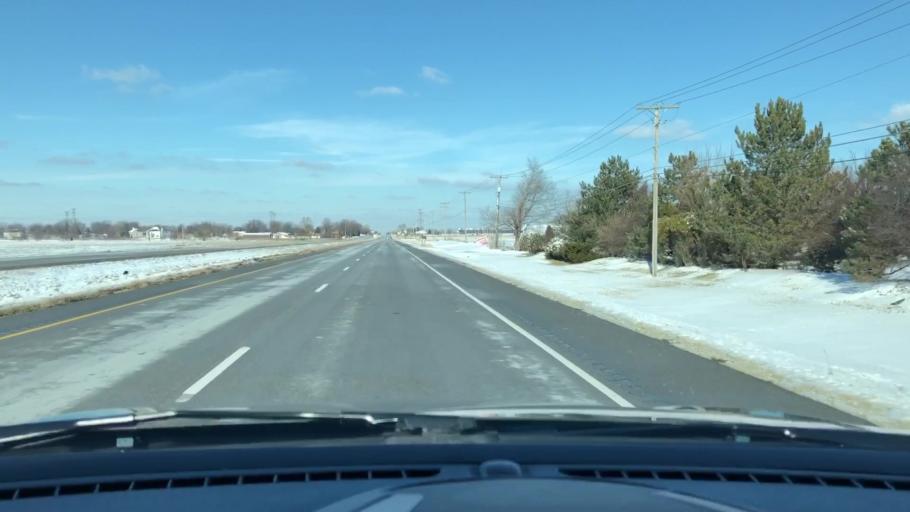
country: US
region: Illinois
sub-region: Will County
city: Elwood
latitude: 41.4399
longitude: -88.0787
